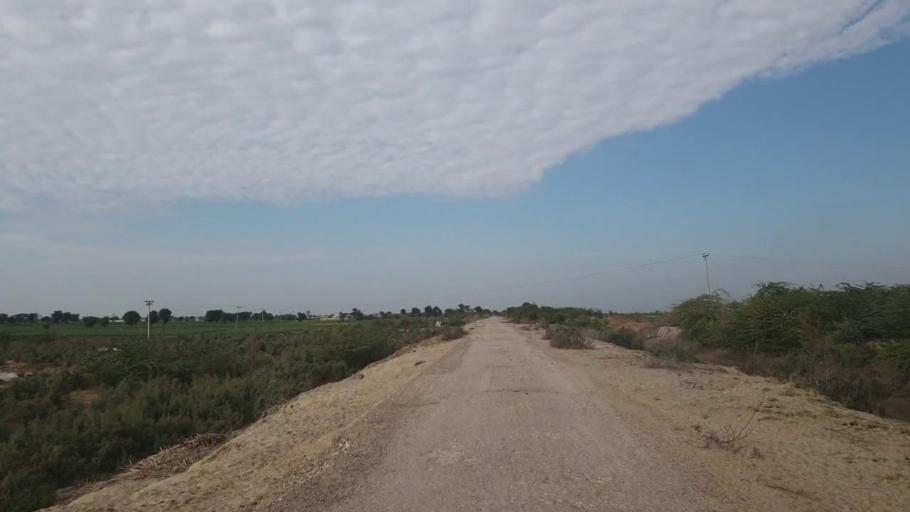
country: PK
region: Sindh
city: Sinjhoro
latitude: 26.0578
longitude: 68.8742
